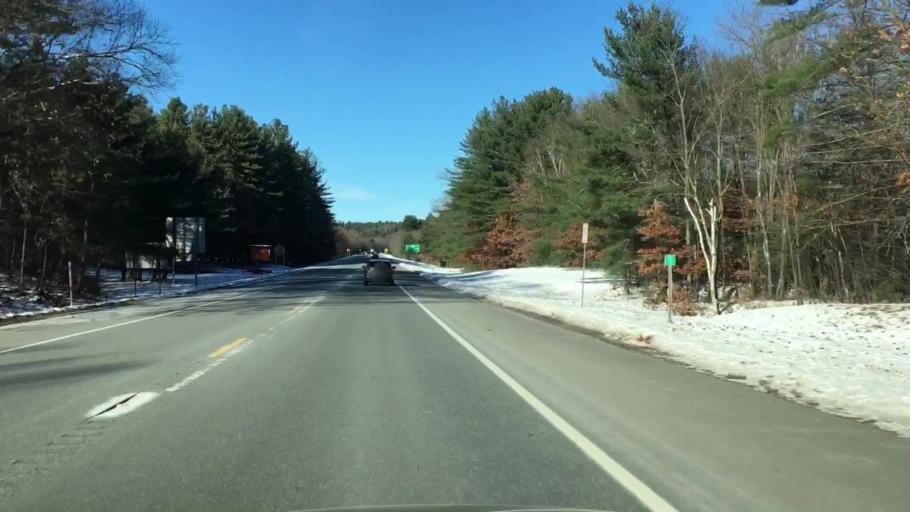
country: US
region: New Hampshire
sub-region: Hillsborough County
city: Milford
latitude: 42.8310
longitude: -71.6178
